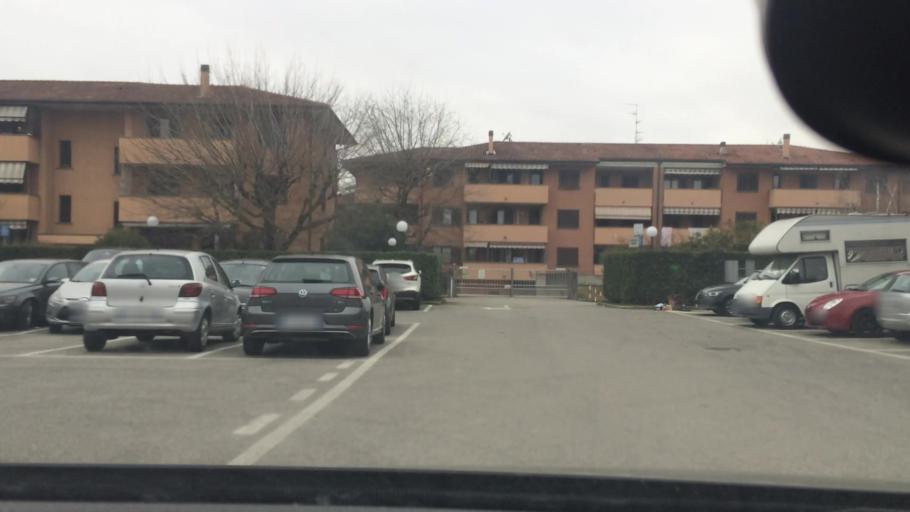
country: IT
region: Lombardy
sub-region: Citta metropolitana di Milano
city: Solaro
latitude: 45.6150
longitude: 9.0744
